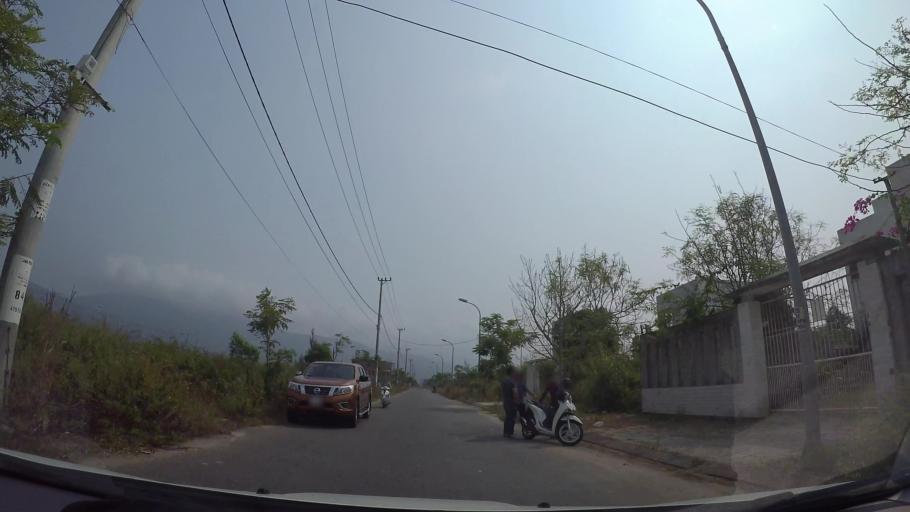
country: VN
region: Da Nang
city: Da Nang
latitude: 16.1001
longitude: 108.2284
